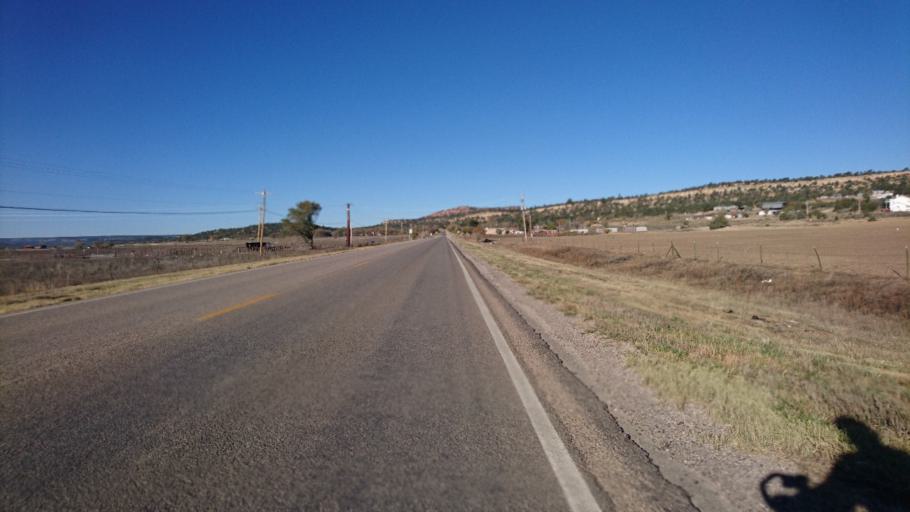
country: US
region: New Mexico
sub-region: McKinley County
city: Black Rock
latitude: 35.1333
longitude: -108.5034
